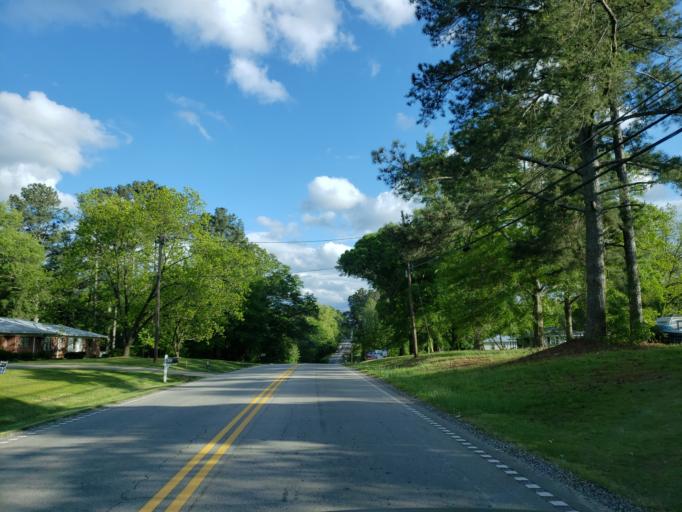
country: US
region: Georgia
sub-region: Haralson County
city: Tallapoosa
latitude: 33.7597
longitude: -85.2935
